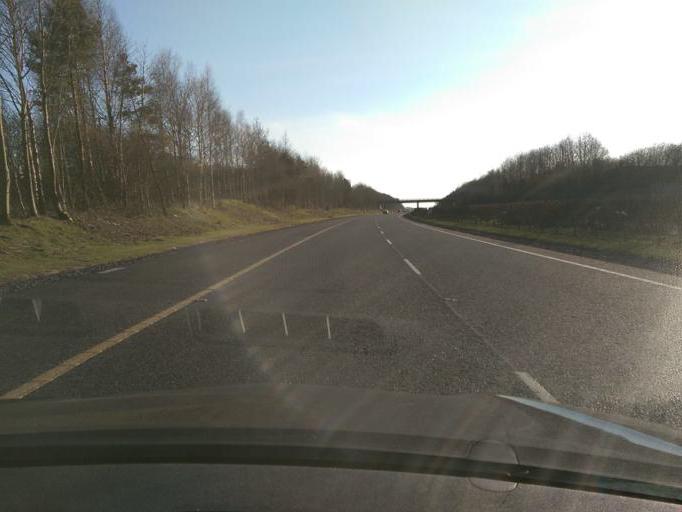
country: IE
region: Leinster
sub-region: Laois
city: Portlaoise
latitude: 53.0333
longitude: -7.2476
